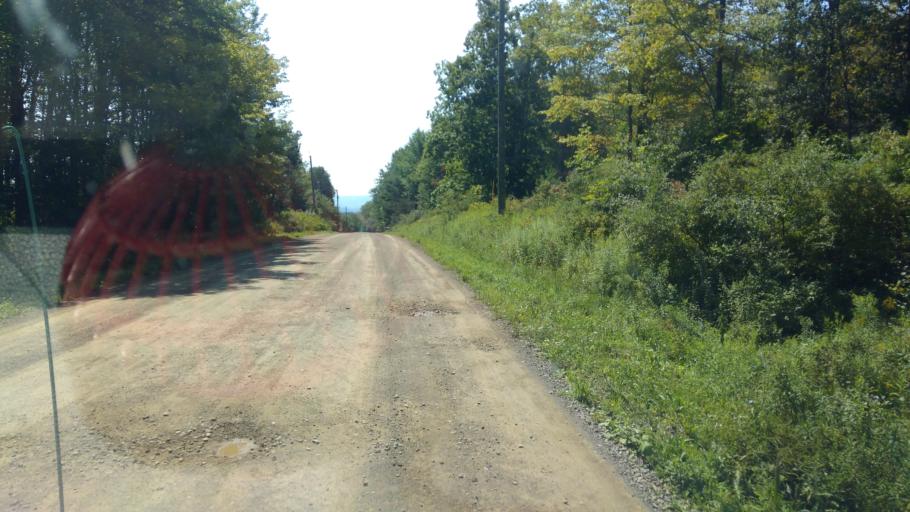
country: US
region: New York
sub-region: Allegany County
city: Belmont
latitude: 42.3504
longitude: -78.0416
